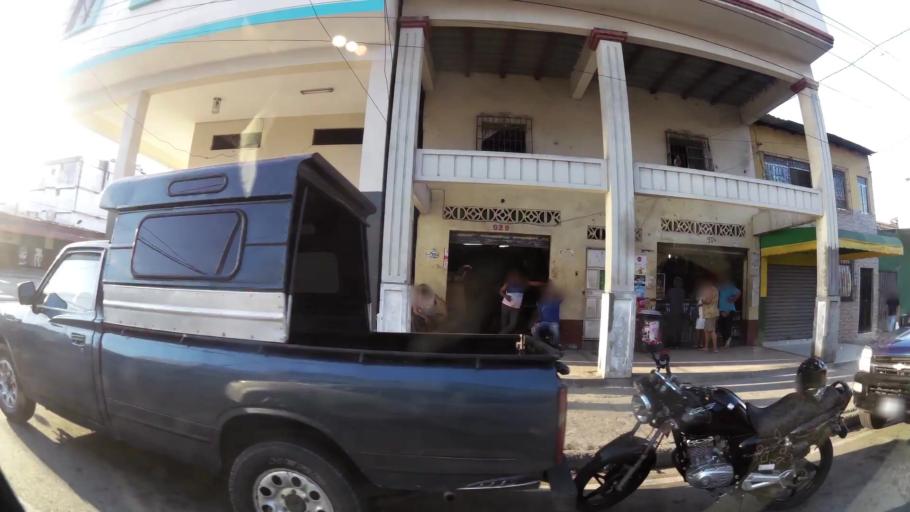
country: EC
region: Guayas
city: Guayaquil
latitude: -2.2088
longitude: -79.8907
